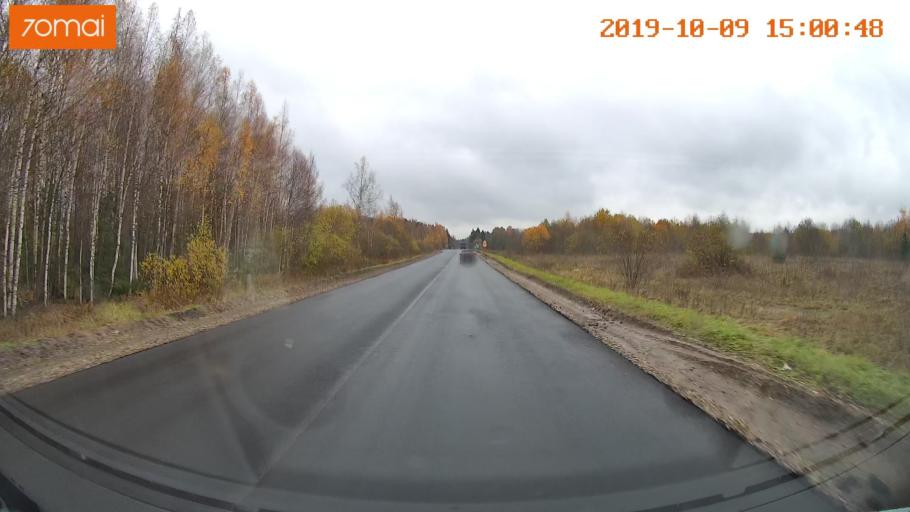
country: RU
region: Kostroma
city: Chistyye Bory
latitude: 58.3051
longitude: 41.6792
